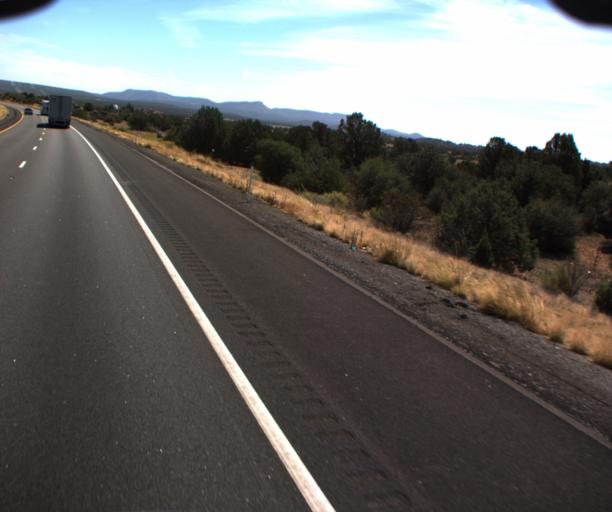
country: US
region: Arizona
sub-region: Mohave County
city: Peach Springs
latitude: 35.1836
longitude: -113.3875
